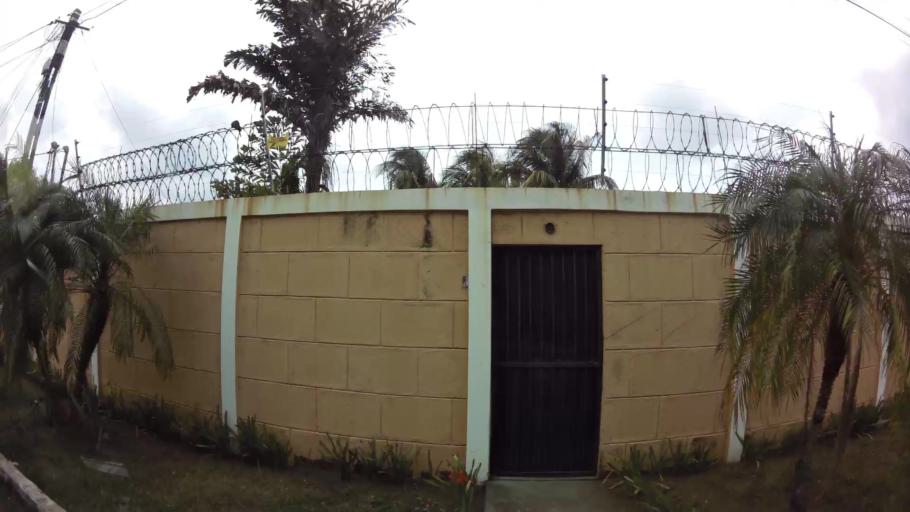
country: NI
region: Managua
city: Managua
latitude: 12.0962
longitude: -86.2269
